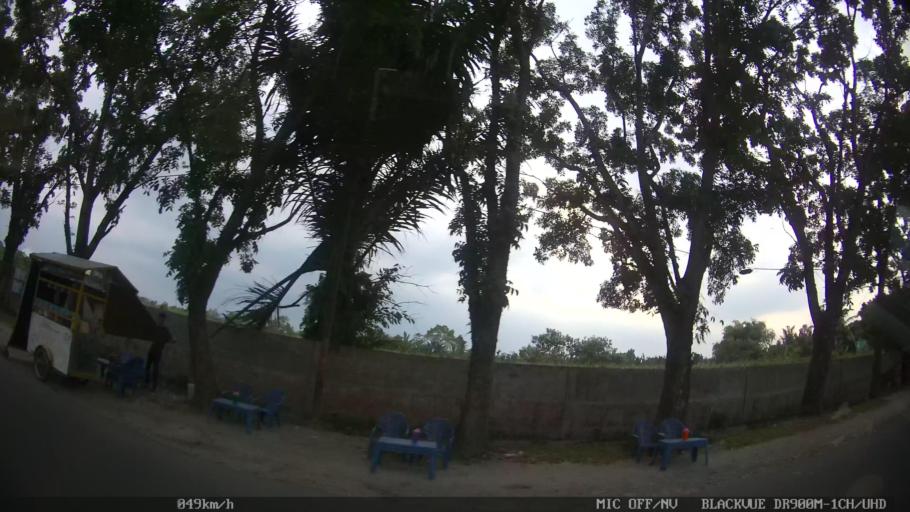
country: ID
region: North Sumatra
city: Sunggal
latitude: 3.5635
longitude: 98.6159
